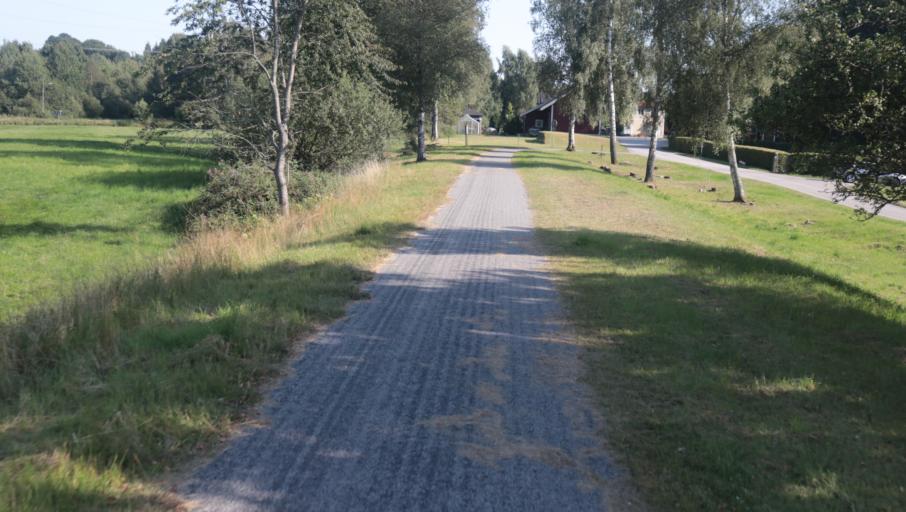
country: SE
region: Blekinge
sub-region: Karlshamns Kommun
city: Svangsta
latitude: 56.3887
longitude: 14.6751
